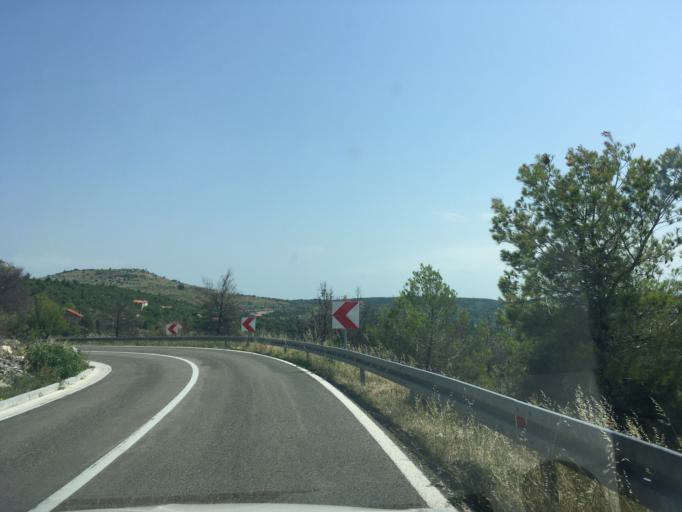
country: HR
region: Sibensko-Kniniska
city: Kistanje
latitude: 43.9399
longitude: 15.8320
